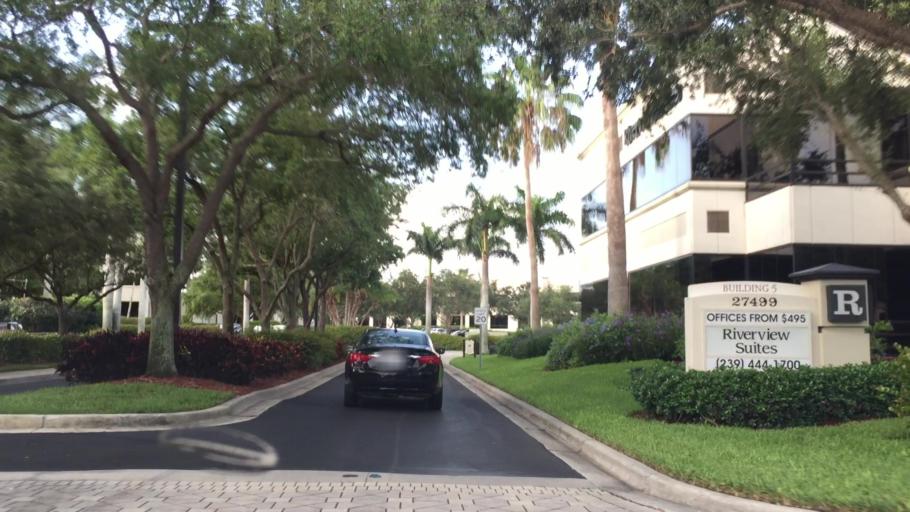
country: US
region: Florida
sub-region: Lee County
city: Bonita Springs
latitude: 26.3416
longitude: -81.8086
